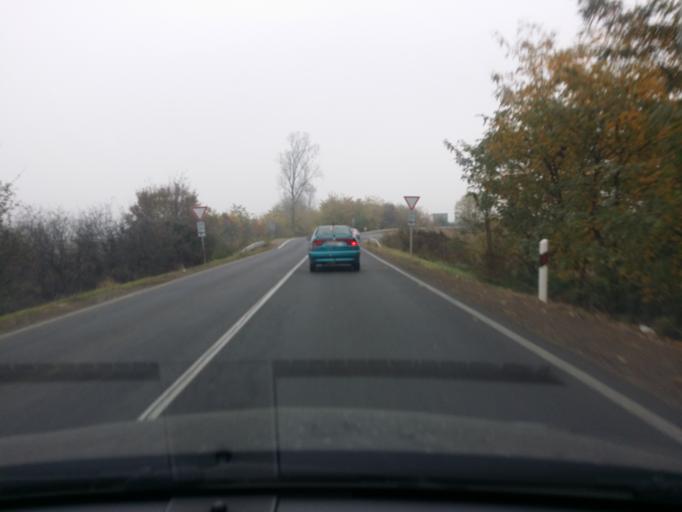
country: HU
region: Szabolcs-Szatmar-Bereg
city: Nyirpazony
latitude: 48.0199
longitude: 21.8415
